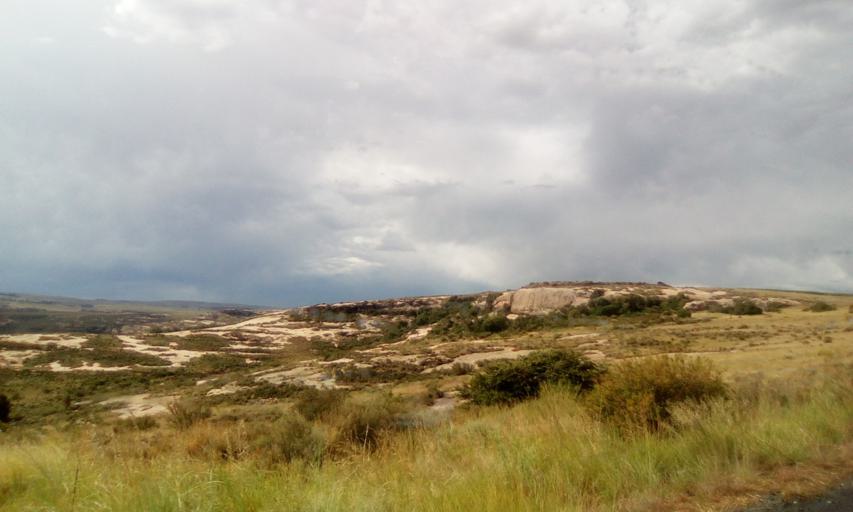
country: ZA
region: Orange Free State
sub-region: Thabo Mofutsanyana District Municipality
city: Ladybrand
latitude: -29.2475
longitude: 27.4444
